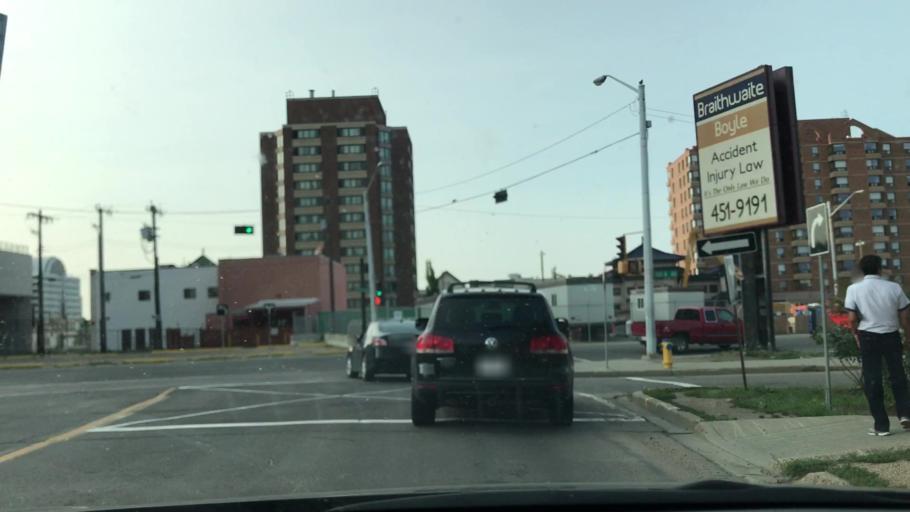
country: CA
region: Alberta
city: Edmonton
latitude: 53.5438
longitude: -113.4807
